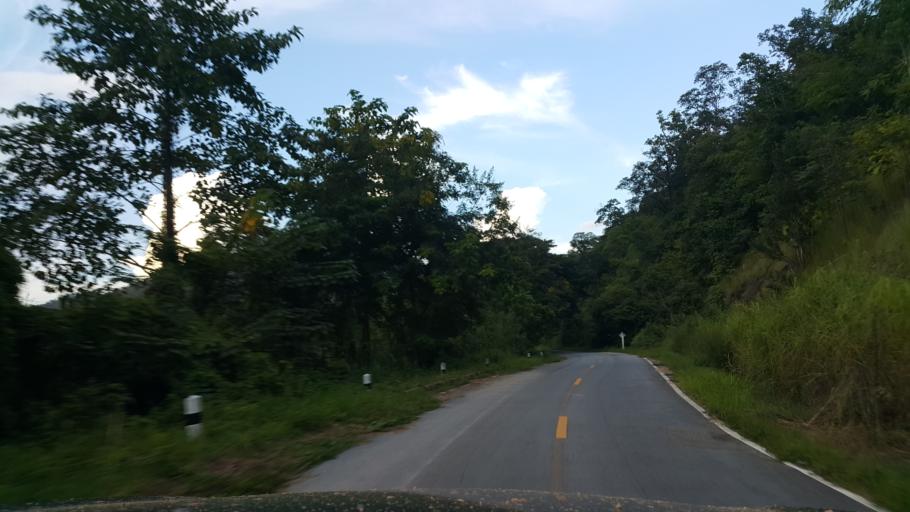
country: TH
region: Mae Hong Son
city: Mae Hi
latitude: 19.2421
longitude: 98.4515
